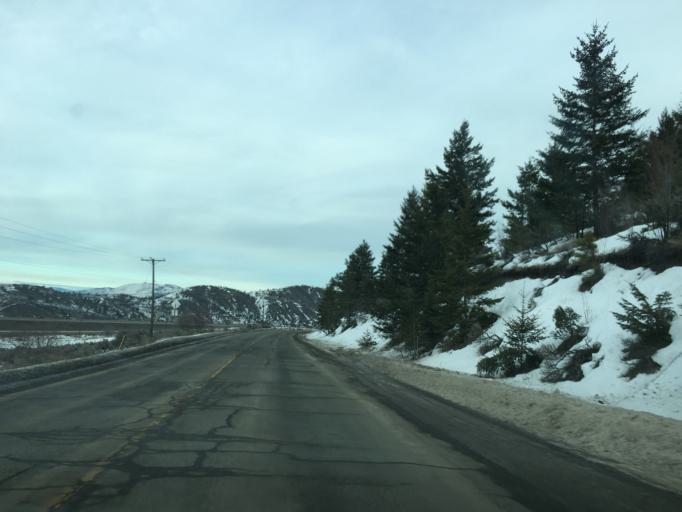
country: CA
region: British Columbia
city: Kamloops
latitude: 50.6628
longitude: -120.4334
